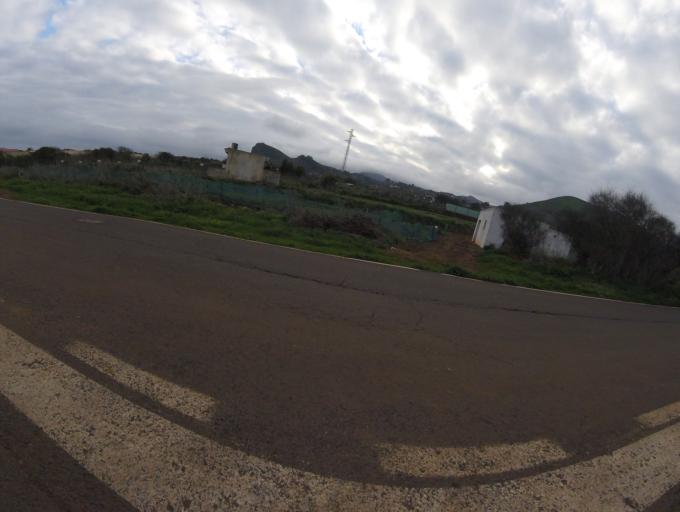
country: ES
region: Canary Islands
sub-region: Provincia de Santa Cruz de Tenerife
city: La Laguna
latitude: 28.4560
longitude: -16.3431
